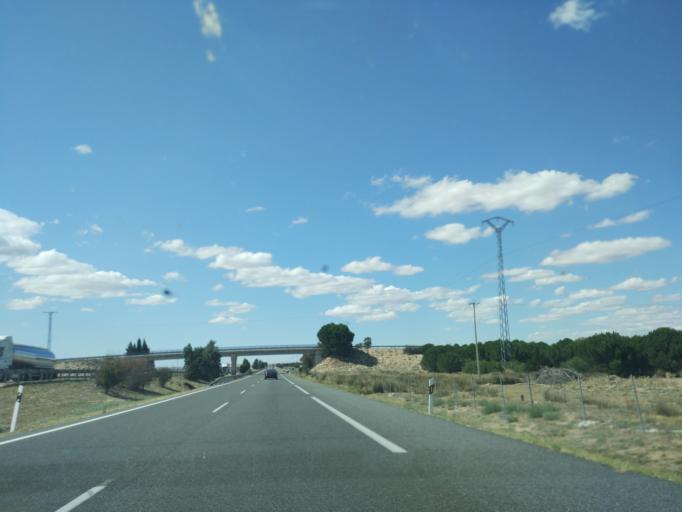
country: ES
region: Castille and Leon
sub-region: Provincia de Valladolid
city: San Vicente del Palacio
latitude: 41.2490
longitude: -4.8695
